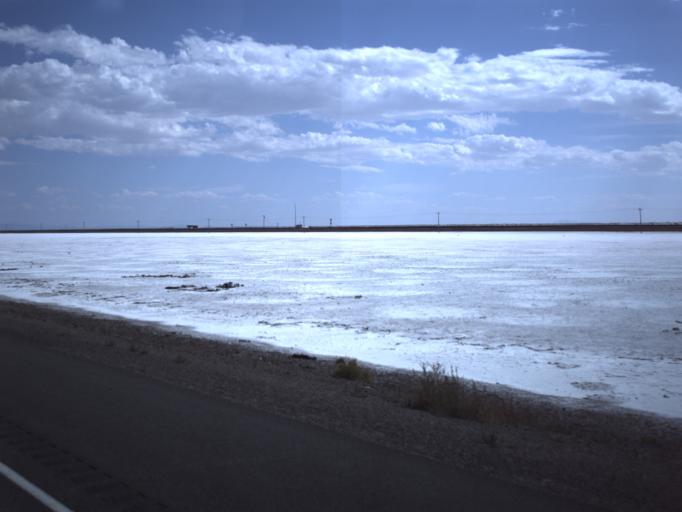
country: US
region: Utah
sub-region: Tooele County
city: Wendover
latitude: 40.7390
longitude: -113.8766
